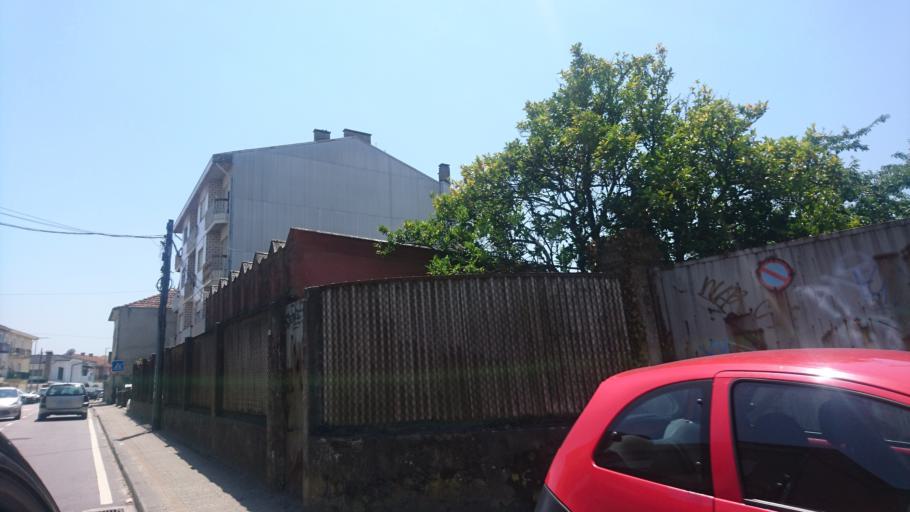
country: PT
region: Porto
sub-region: Gondomar
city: Rio Tinto
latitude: 41.1659
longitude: -8.5470
